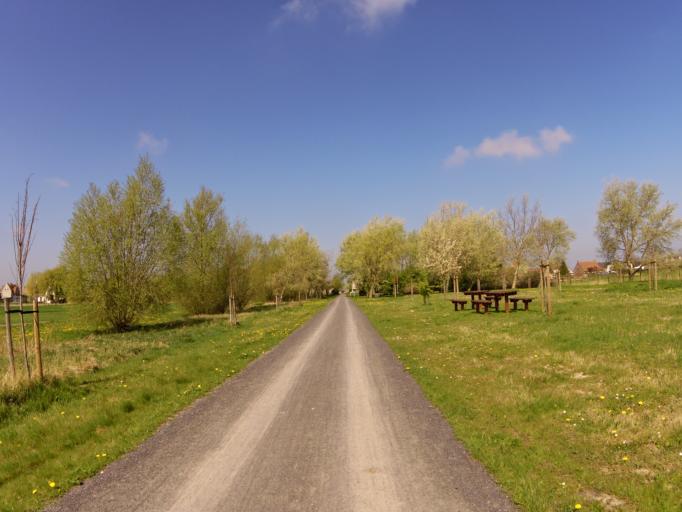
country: BE
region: Flanders
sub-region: Provincie West-Vlaanderen
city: Nieuwpoort
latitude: 51.0733
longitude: 2.8003
